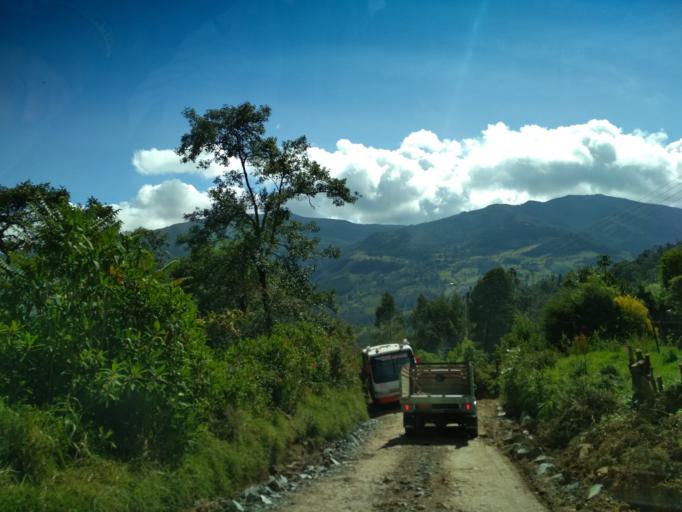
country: CO
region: Cauca
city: Jambalo
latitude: 2.7090
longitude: -76.3297
